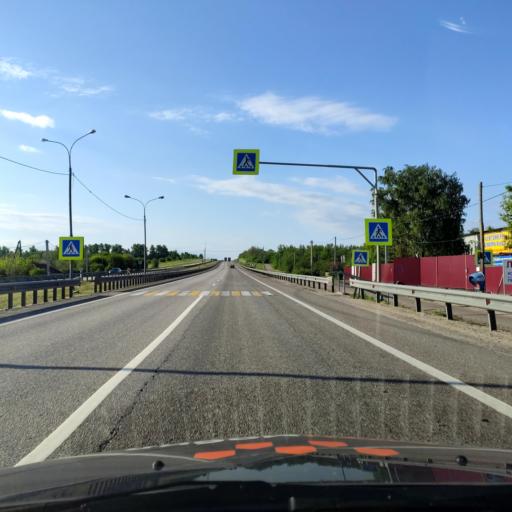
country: RU
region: Voronezj
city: Ramon'
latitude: 52.0371
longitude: 39.1986
